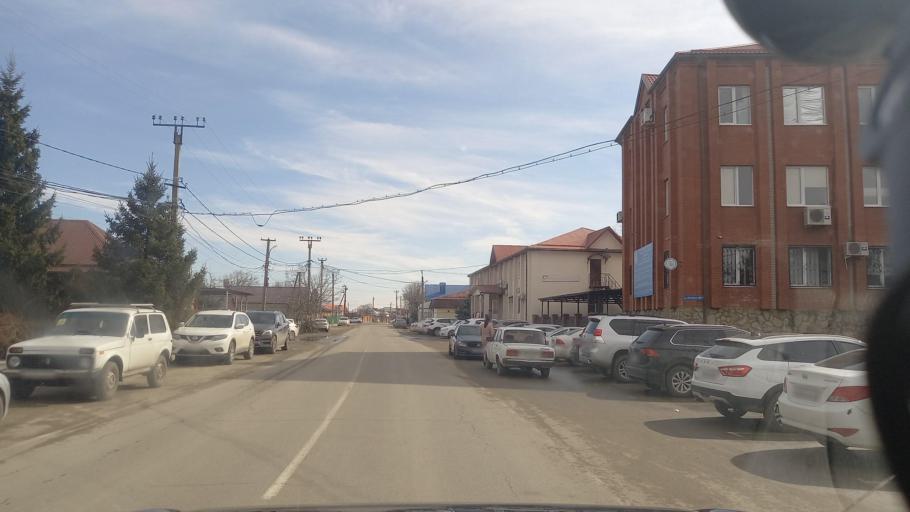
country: RU
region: Adygeya
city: Takhtamukay
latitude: 44.9257
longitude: 38.9909
